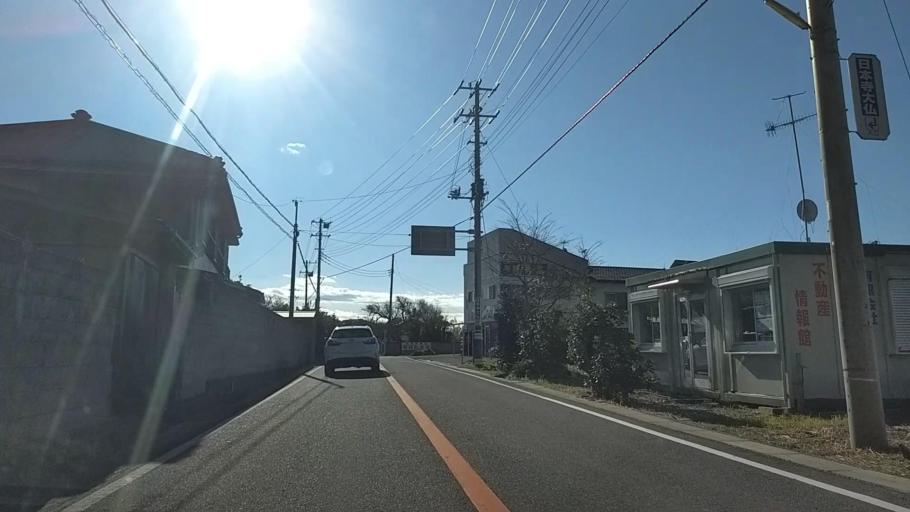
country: JP
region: Chiba
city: Futtsu
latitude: 35.1506
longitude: 139.8301
